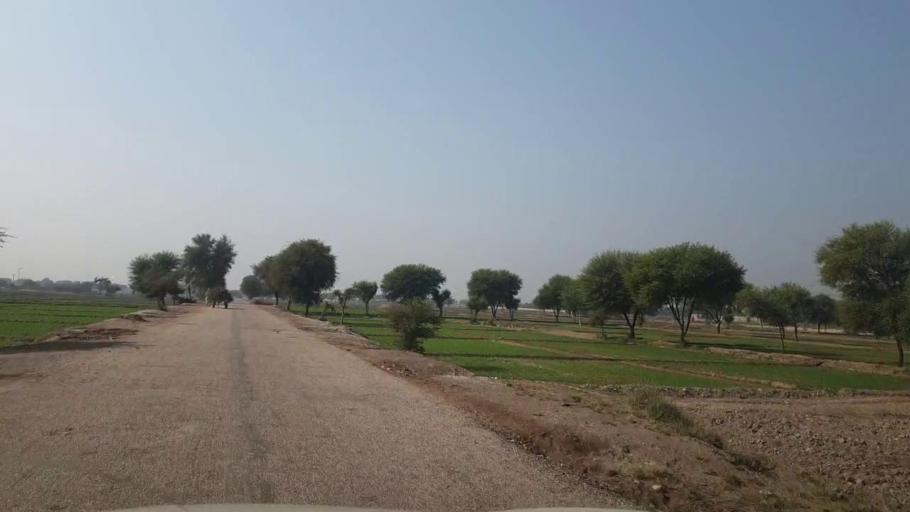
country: PK
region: Sindh
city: Bhan
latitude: 26.5113
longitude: 67.7956
